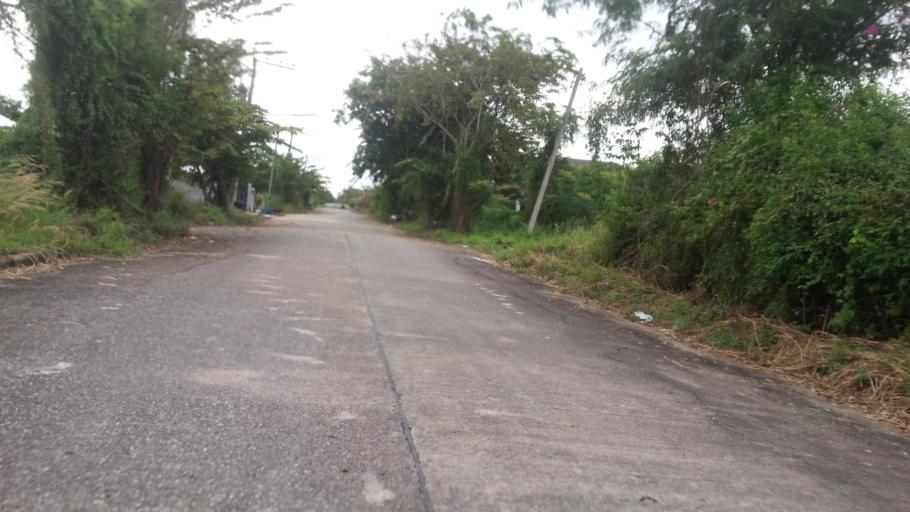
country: TH
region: Pathum Thani
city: Nong Suea
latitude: 14.0643
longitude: 100.8784
